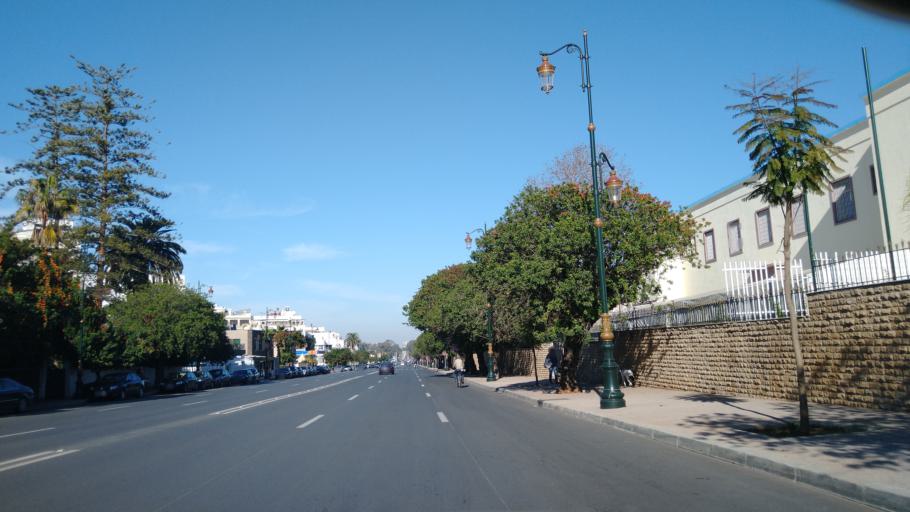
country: MA
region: Rabat-Sale-Zemmour-Zaer
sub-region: Rabat
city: Rabat
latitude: 33.9940
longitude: -6.8454
